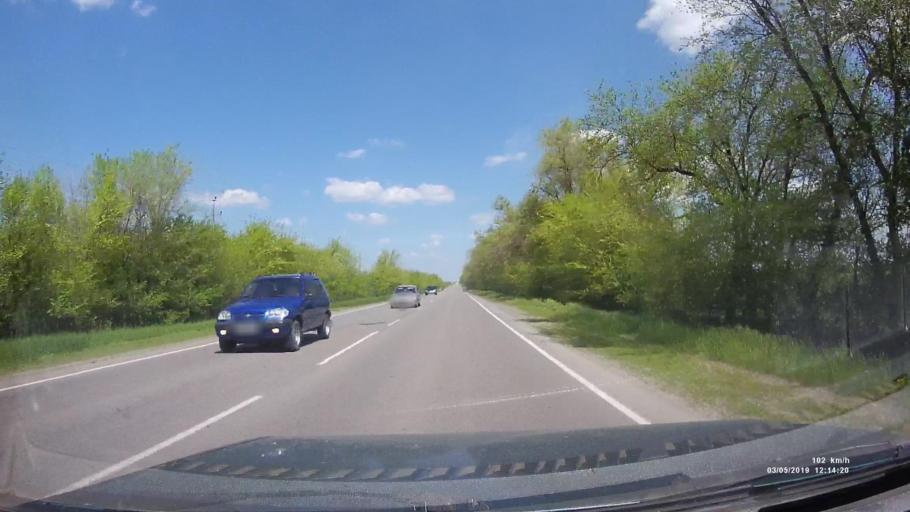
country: RU
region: Rostov
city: Melikhovskaya
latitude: 47.3427
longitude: 40.5624
